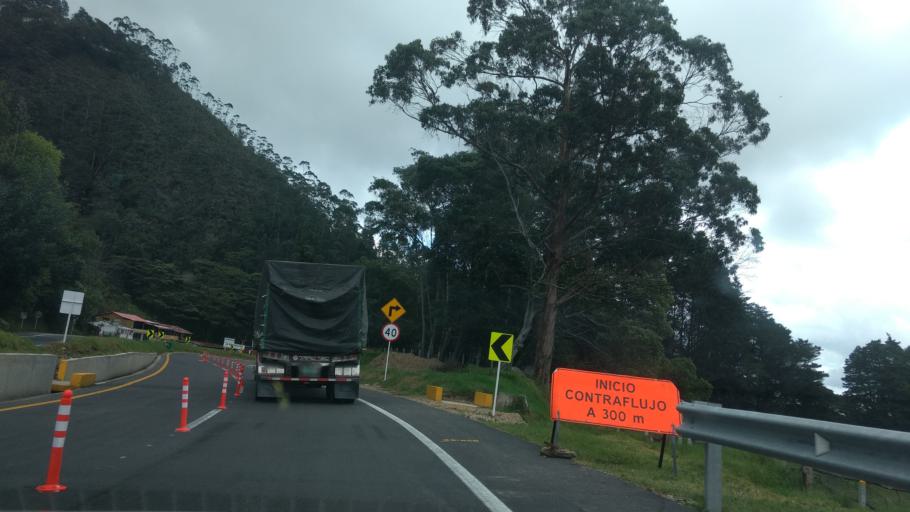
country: CO
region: Cundinamarca
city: San Francisco
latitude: 4.9241
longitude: -74.2916
